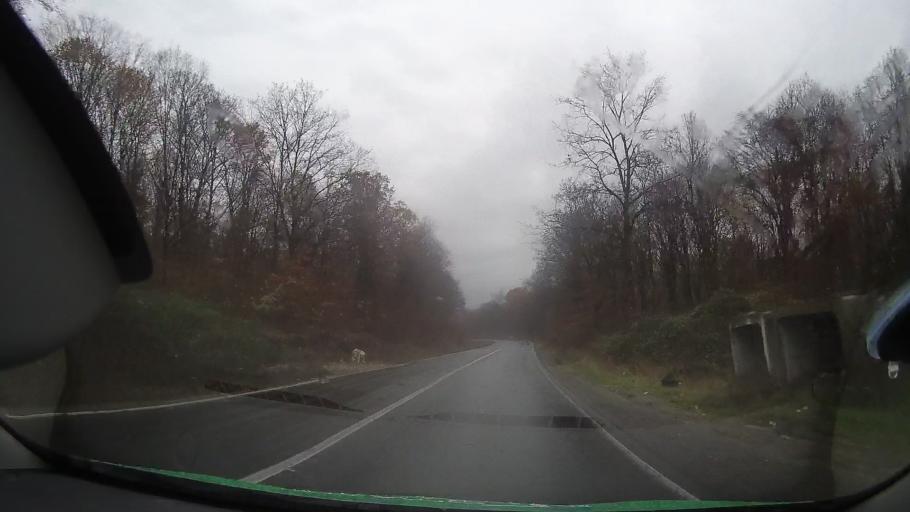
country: RO
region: Bihor
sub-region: Comuna Rabagani
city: Rabagani
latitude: 46.7334
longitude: 22.2304
